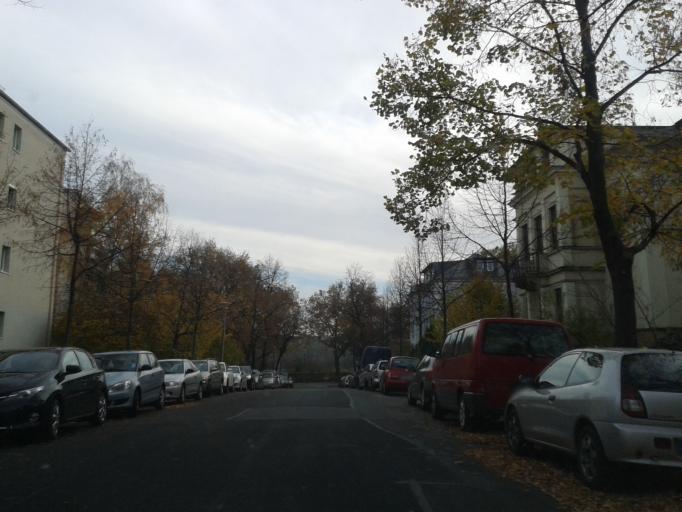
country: DE
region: Saxony
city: Dresden
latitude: 51.0616
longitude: 13.7564
